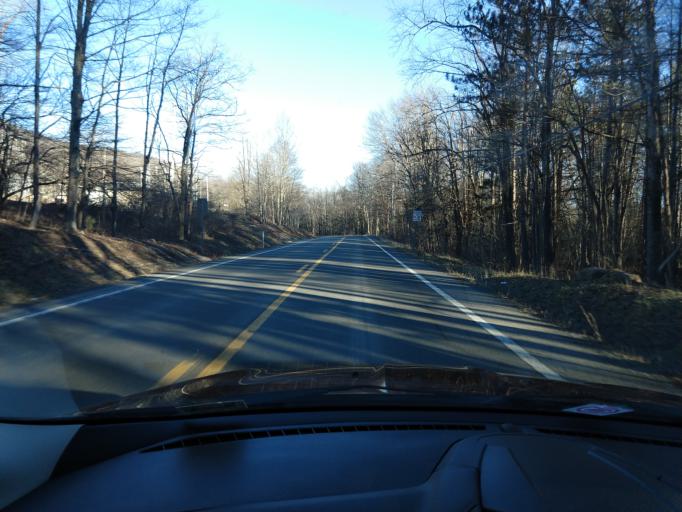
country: US
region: Virginia
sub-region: Highland County
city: Monterey
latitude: 38.5744
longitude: -79.8403
